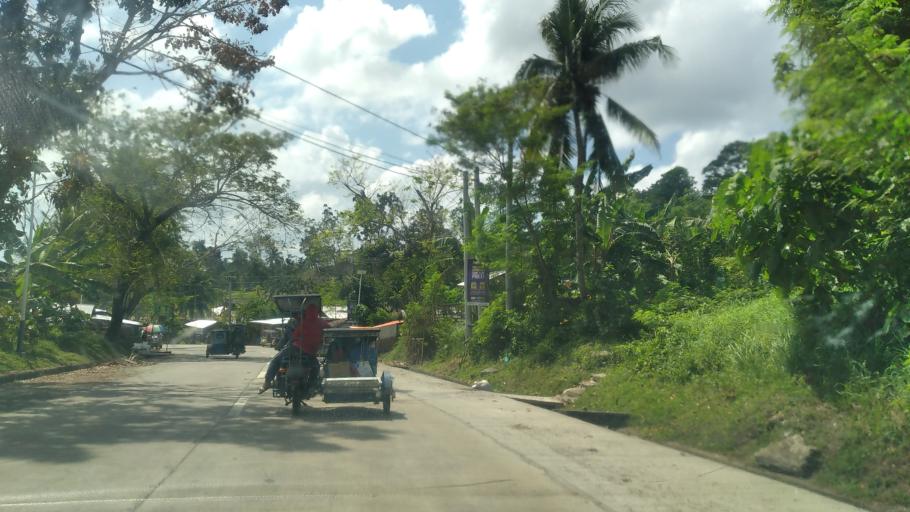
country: PH
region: Calabarzon
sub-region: Province of Quezon
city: Macalelon
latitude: 13.7588
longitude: 122.1418
